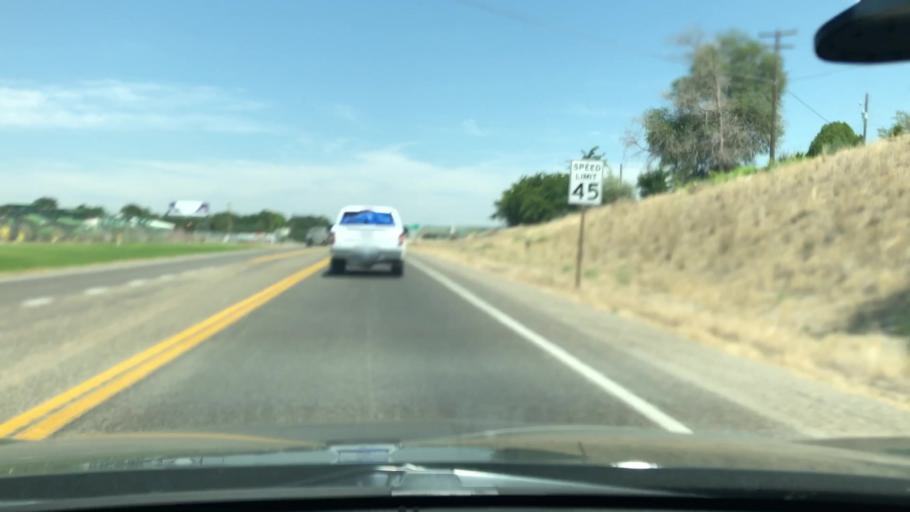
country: US
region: Idaho
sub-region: Owyhee County
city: Homedale
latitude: 43.6210
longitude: -116.9206
